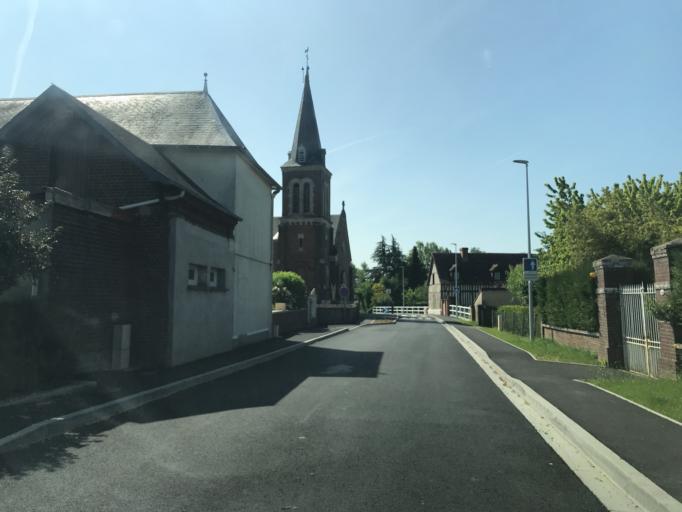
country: FR
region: Haute-Normandie
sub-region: Departement de la Seine-Maritime
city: Belbeuf
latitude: 49.3667
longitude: 1.1585
